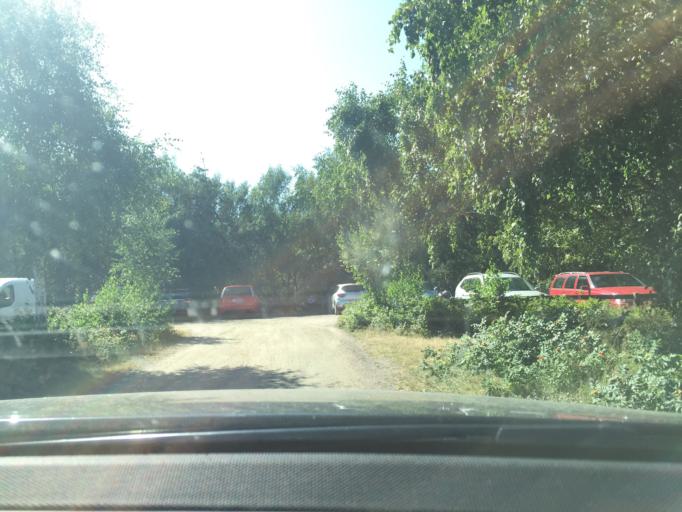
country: SE
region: Halland
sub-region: Laholms Kommun
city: Mellbystrand
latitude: 56.5055
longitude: 12.9426
